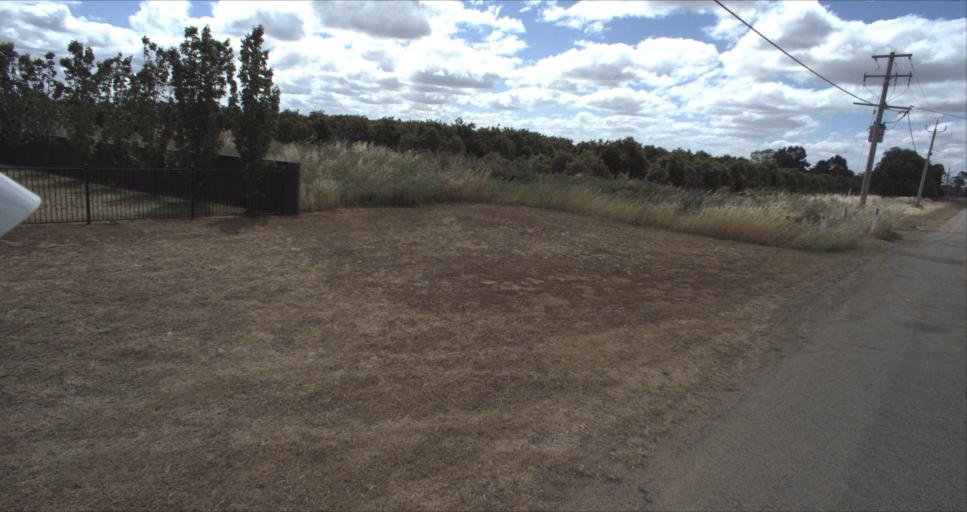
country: AU
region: New South Wales
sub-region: Leeton
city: Leeton
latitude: -34.5844
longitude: 146.3963
